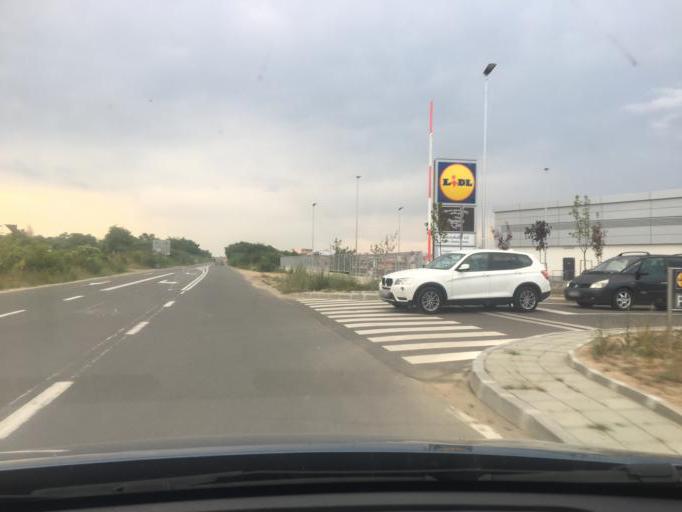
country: BG
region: Burgas
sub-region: Obshtina Sozopol
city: Sozopol
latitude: 42.4058
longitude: 27.7060
